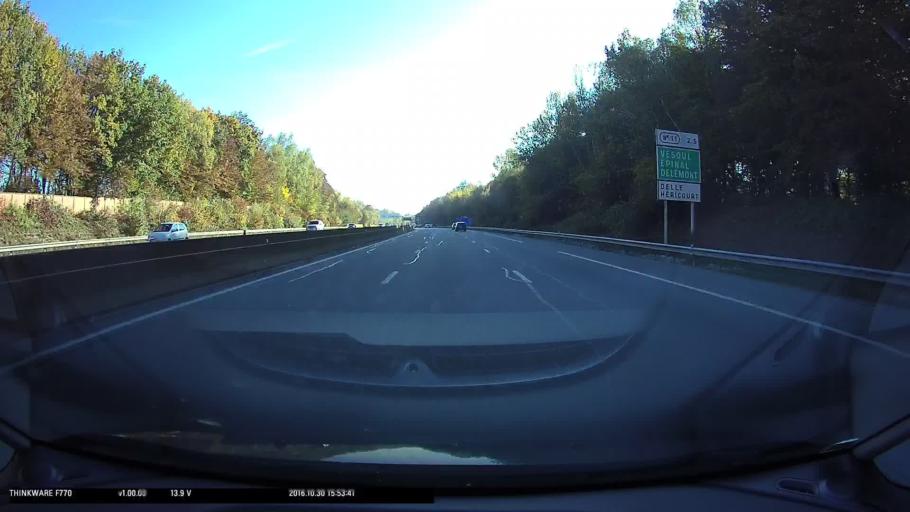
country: FR
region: Franche-Comte
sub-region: Territoire de Belfort
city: Danjoutin
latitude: 47.6118
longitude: 6.8561
